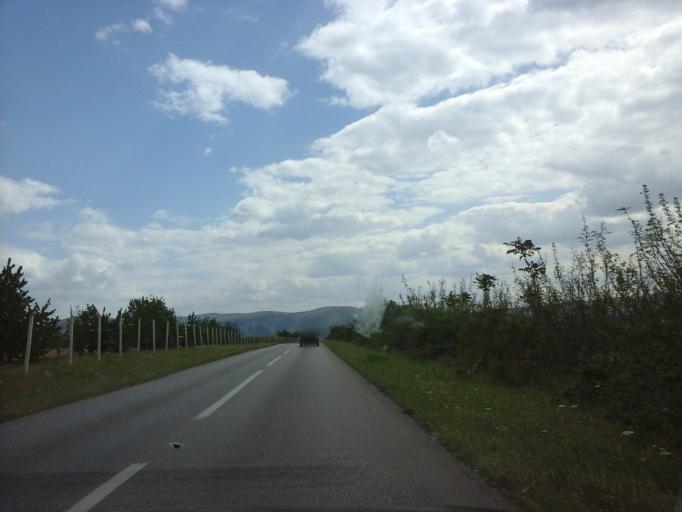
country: BA
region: Federation of Bosnia and Herzegovina
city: Blagaj
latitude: 43.2806
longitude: 17.8530
